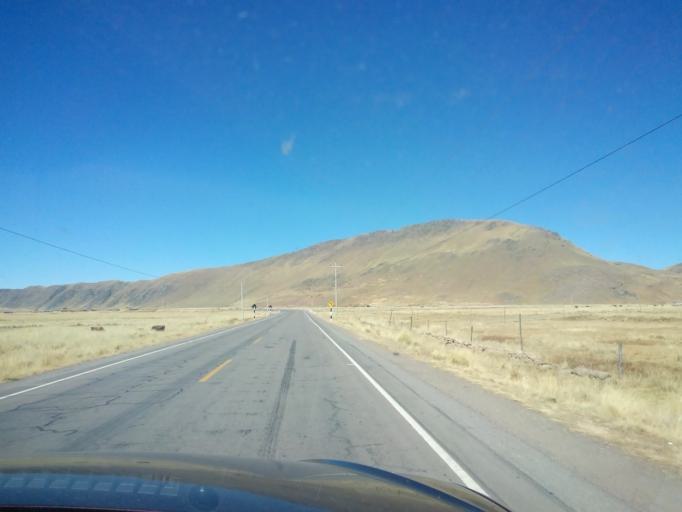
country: PE
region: Puno
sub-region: Provincia de Melgar
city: Santa Rosa
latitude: -14.5847
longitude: -70.8658
